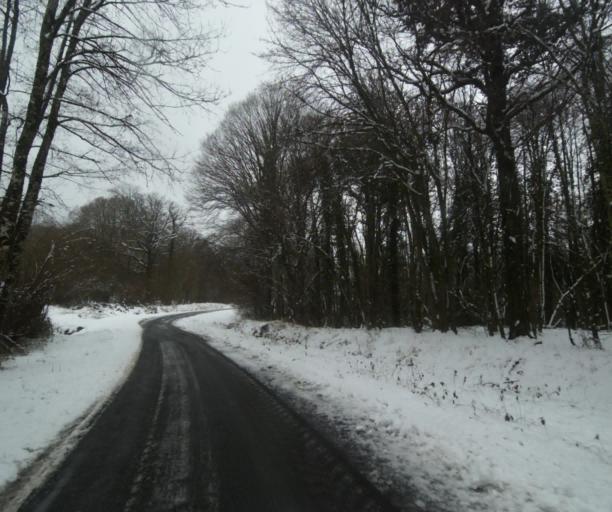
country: FR
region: Champagne-Ardenne
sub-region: Departement de la Haute-Marne
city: Laneuville-a-Remy
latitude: 48.4660
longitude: 4.9014
